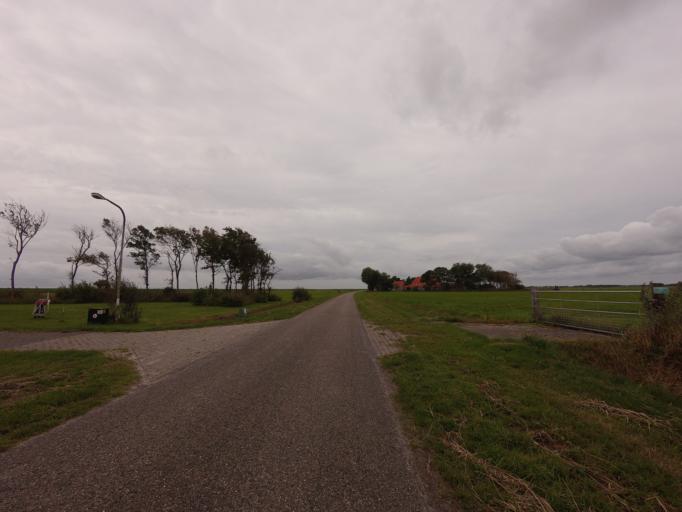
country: NL
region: Friesland
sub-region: Gemeente Ameland
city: Hollum
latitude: 53.4338
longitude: 5.7025
